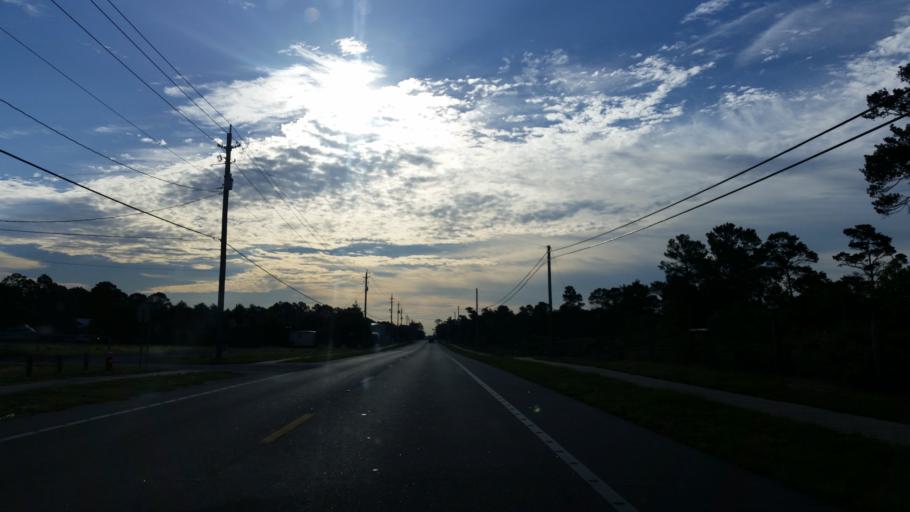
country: US
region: Florida
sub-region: Escambia County
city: Myrtle Grove
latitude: 30.3209
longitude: -87.4091
